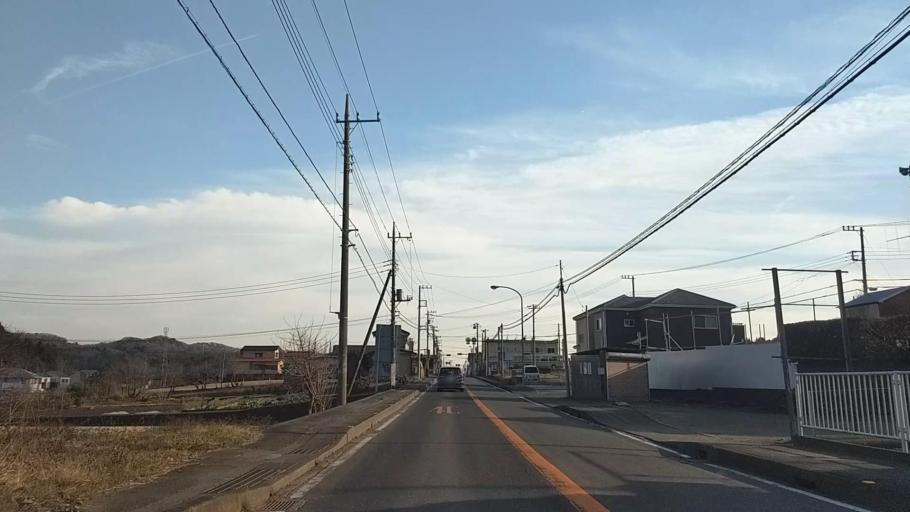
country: JP
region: Kanagawa
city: Zama
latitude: 35.5145
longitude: 139.2987
